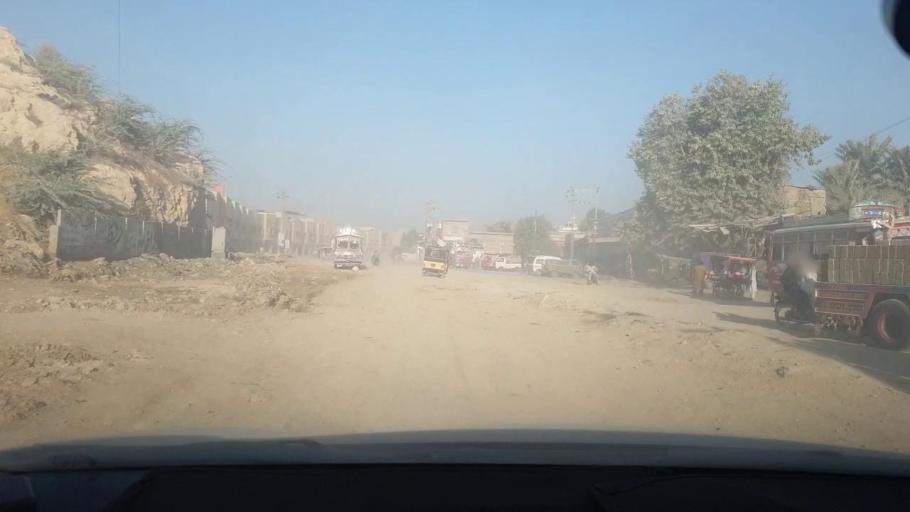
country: PK
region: Sindh
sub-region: Karachi District
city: Karachi
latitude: 24.9764
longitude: 67.0385
